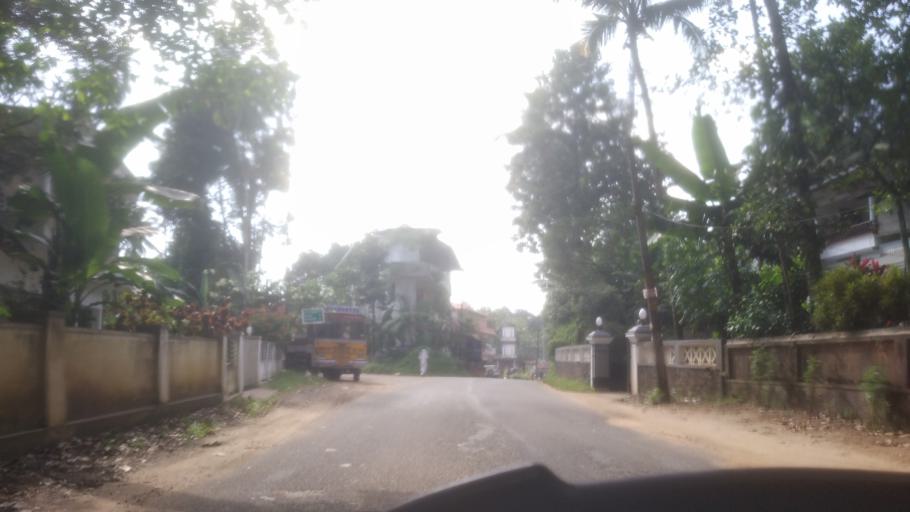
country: IN
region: Kerala
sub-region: Ernakulam
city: Muvattupula
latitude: 9.9980
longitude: 76.6382
